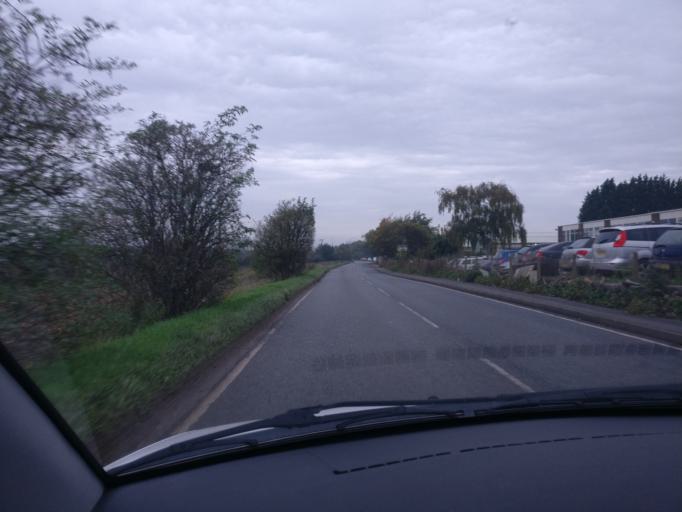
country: GB
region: England
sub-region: Peterborough
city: Eye
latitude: 52.5883
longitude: -0.1999
